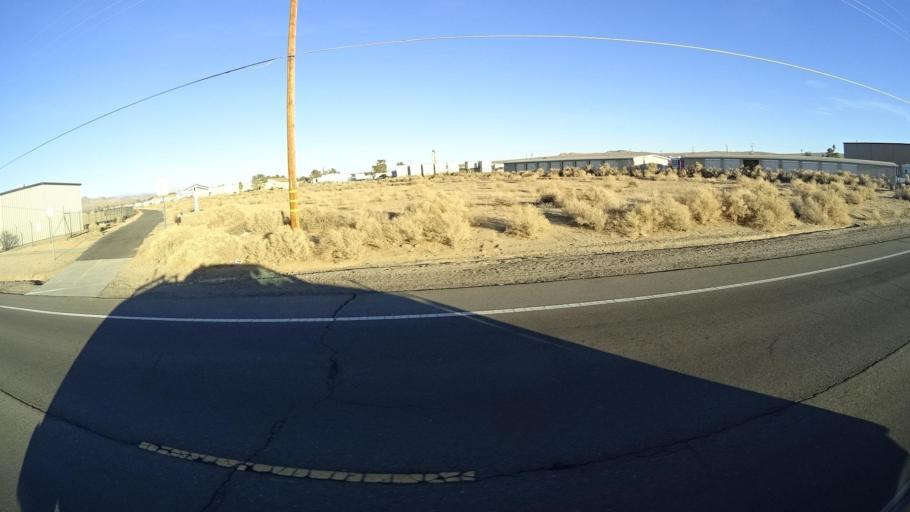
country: US
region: California
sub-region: Kern County
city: Ridgecrest
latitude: 35.6093
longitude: -117.6526
